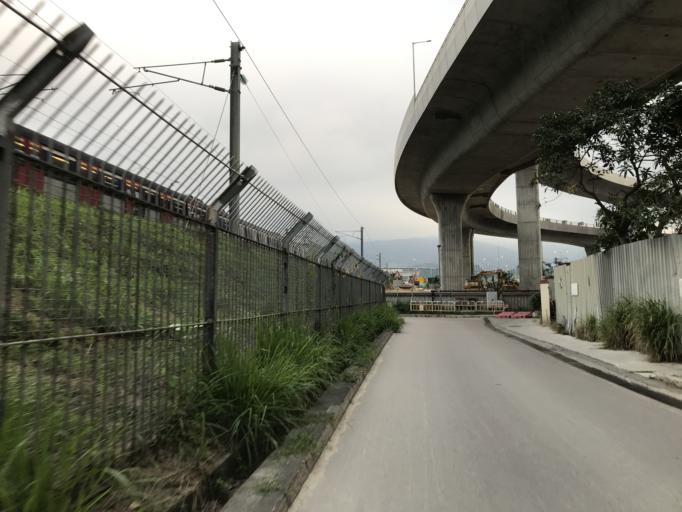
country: HK
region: Tai Po
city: Tai Po
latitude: 22.4792
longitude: 114.1550
